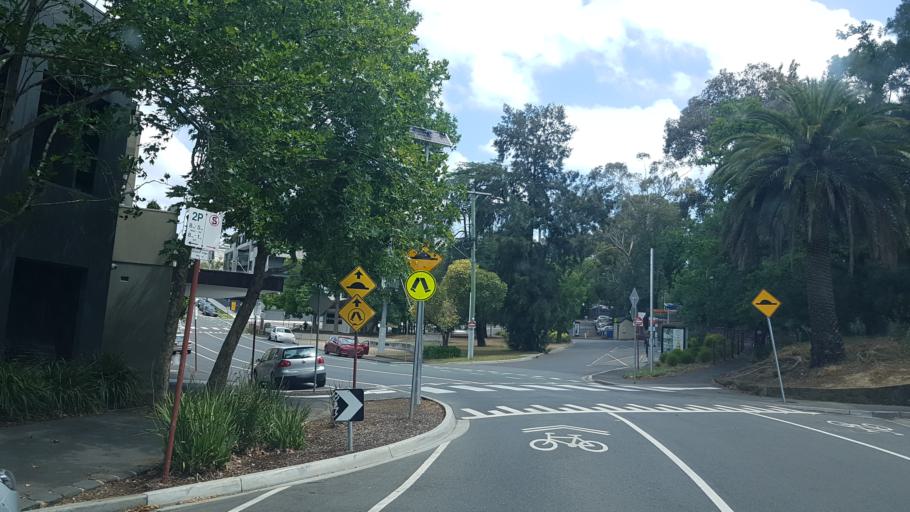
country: AU
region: Victoria
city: Rosanna
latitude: -37.7568
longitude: 145.0621
